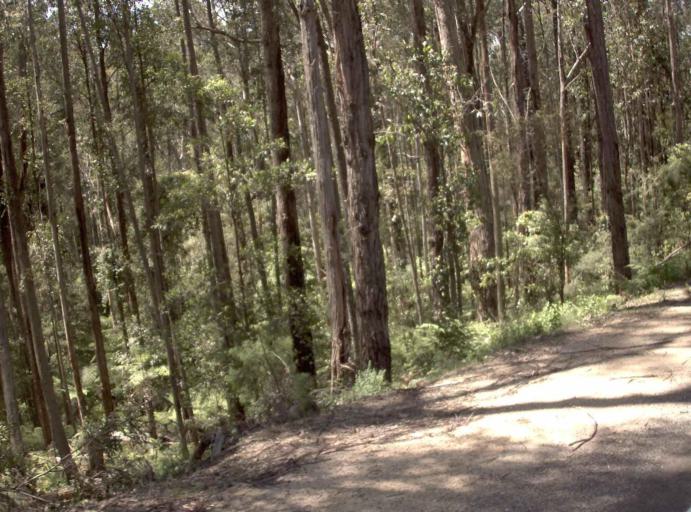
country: AU
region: New South Wales
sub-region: Bombala
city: Bombala
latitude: -37.5850
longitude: 148.9935
